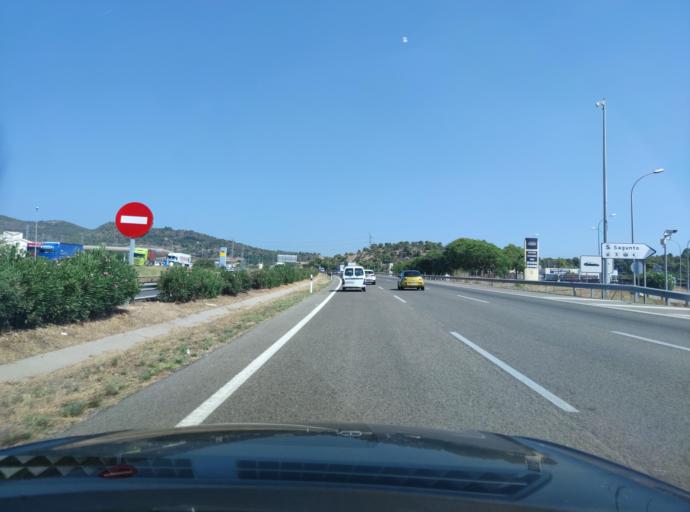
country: ES
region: Valencia
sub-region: Provincia de Valencia
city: Pucol
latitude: 39.6482
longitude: -0.3006
